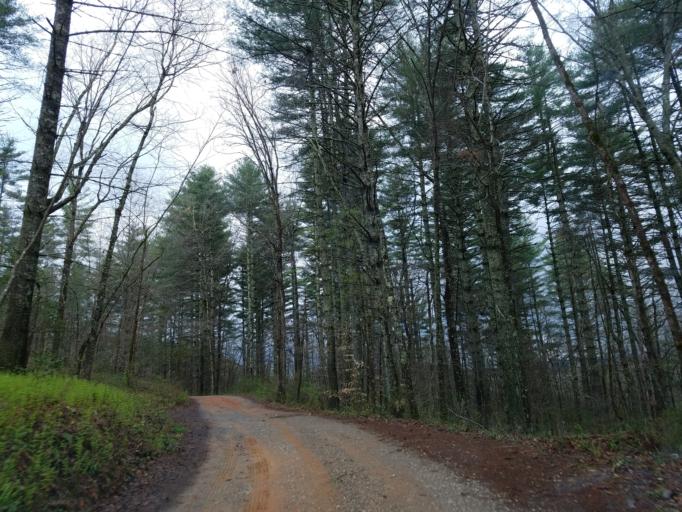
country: US
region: Georgia
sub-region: Fannin County
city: Blue Ridge
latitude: 34.7584
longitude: -84.1746
